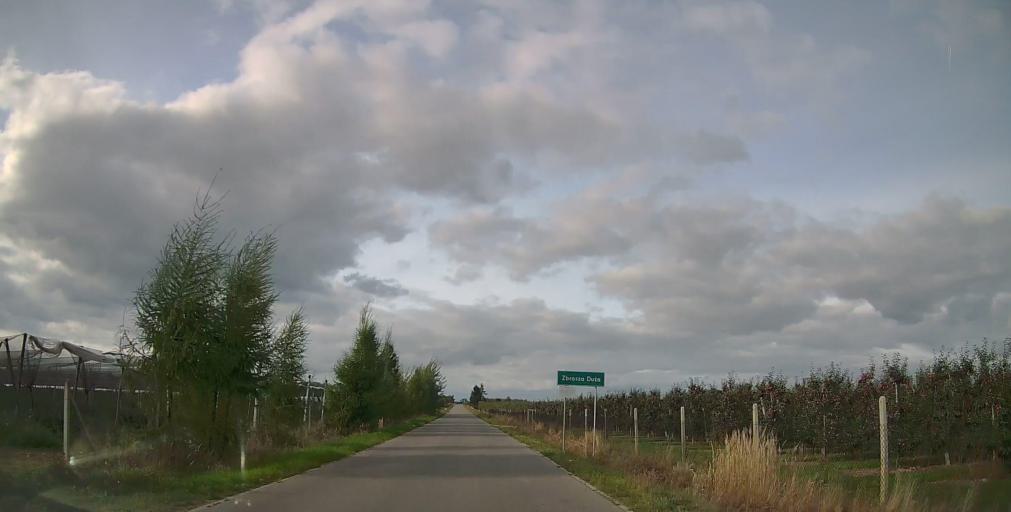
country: PL
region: Masovian Voivodeship
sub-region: Powiat bialobrzeski
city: Promna
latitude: 51.7456
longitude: 20.9641
